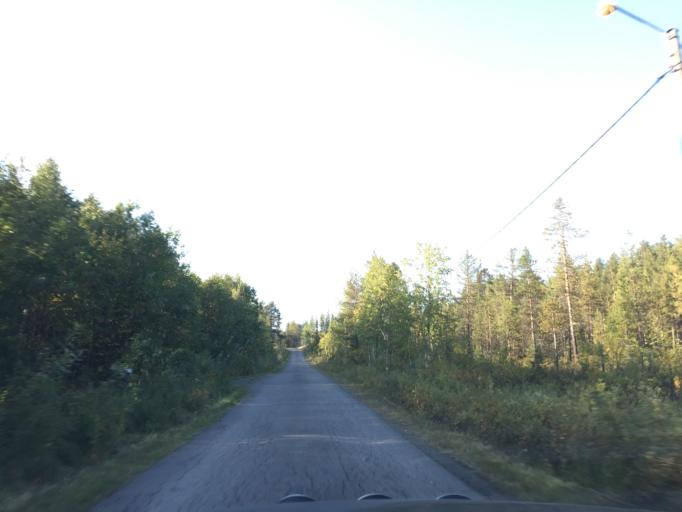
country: SE
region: Norrbotten
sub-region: Gallivare Kommun
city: Malmberget
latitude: 67.6526
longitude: 21.0406
